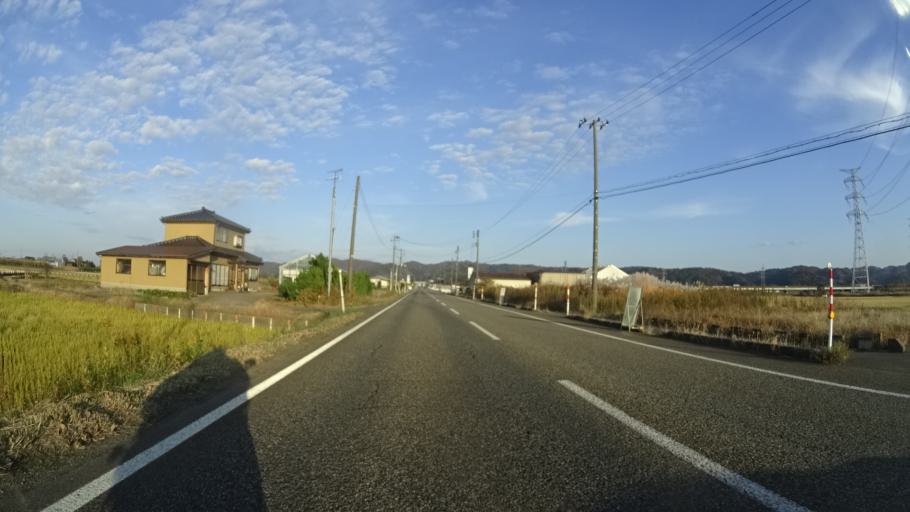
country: JP
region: Niigata
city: Kashiwazaki
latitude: 37.3999
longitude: 138.6190
